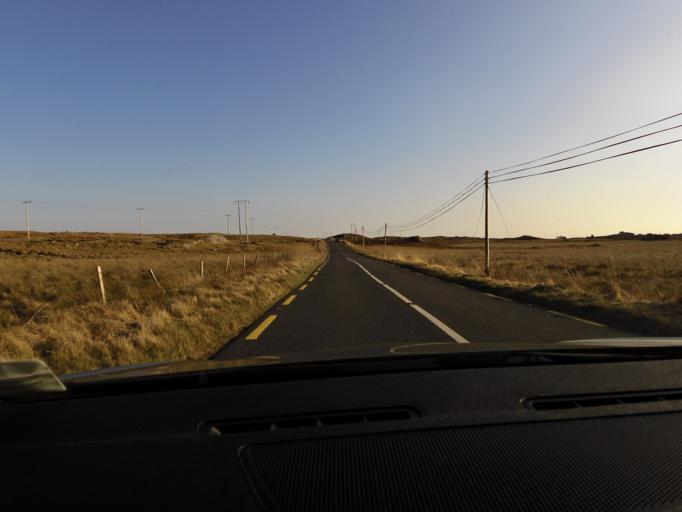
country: IE
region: Connaught
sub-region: County Galway
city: Oughterard
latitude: 53.3614
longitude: -9.5429
